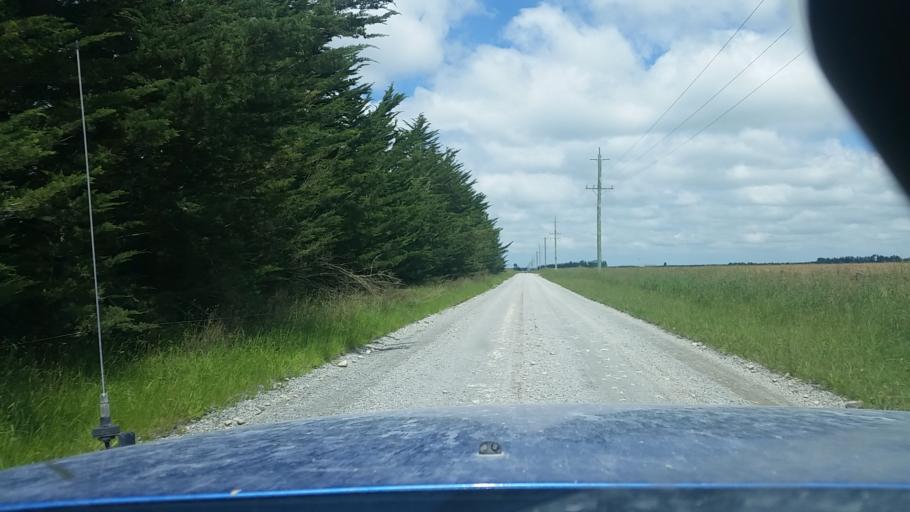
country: NZ
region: Canterbury
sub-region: Ashburton District
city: Tinwald
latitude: -43.8561
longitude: 171.3744
